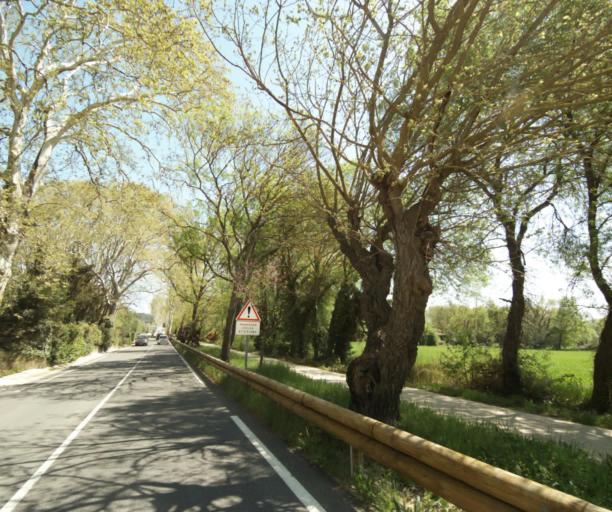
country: FR
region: Languedoc-Roussillon
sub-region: Departement de l'Herault
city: Prades-le-Lez
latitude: 43.7019
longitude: 3.8549
